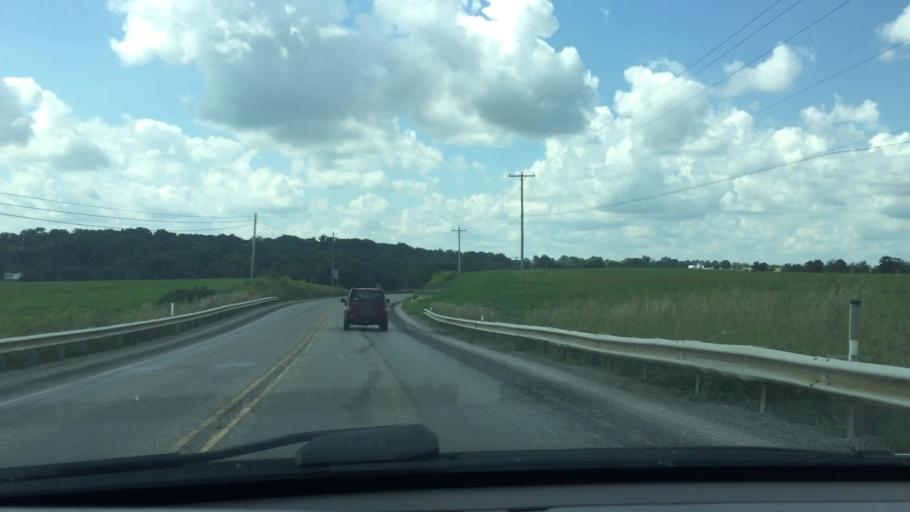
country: US
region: Pennsylvania
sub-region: Lawrence County
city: New Wilmington
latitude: 41.1166
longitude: -80.2747
